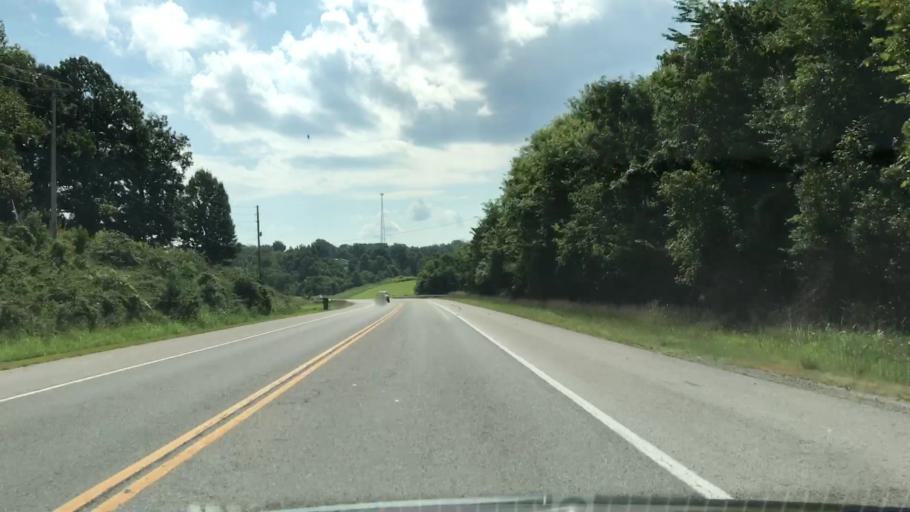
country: US
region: Tennessee
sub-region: Sumner County
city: Westmoreland
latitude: 36.5467
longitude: -86.2205
